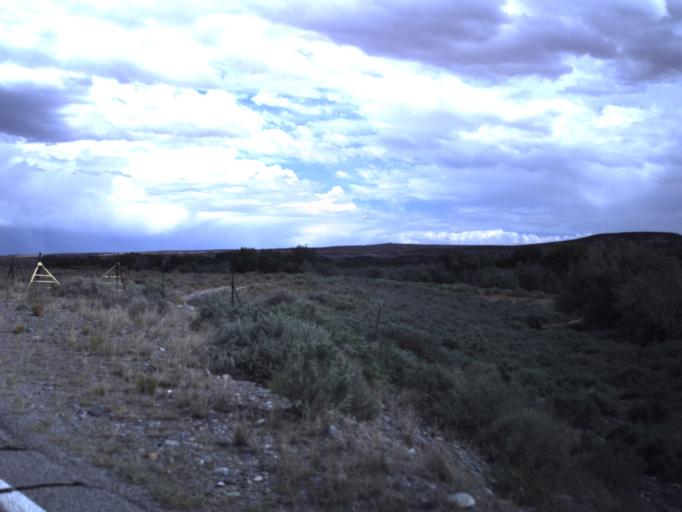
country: US
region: Utah
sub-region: San Juan County
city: Blanding
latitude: 37.2821
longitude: -109.5078
